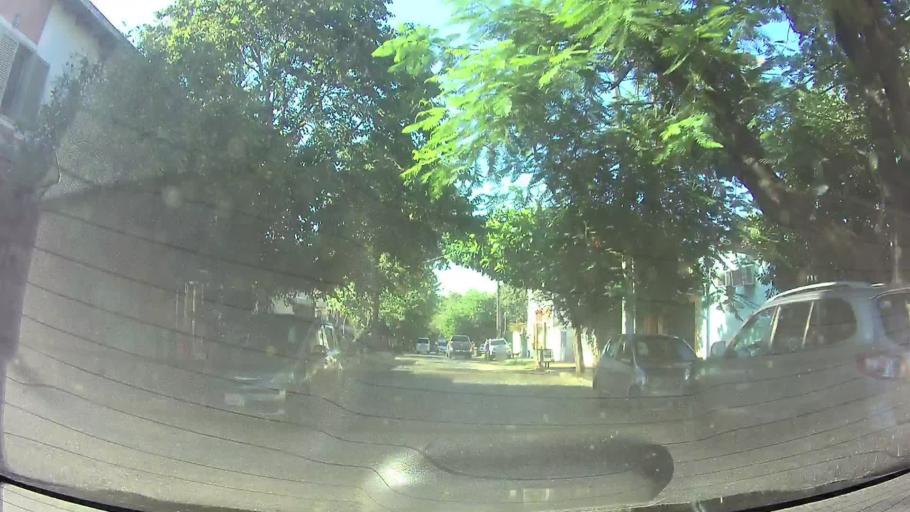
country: PY
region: Asuncion
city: Asuncion
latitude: -25.2820
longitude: -57.5990
